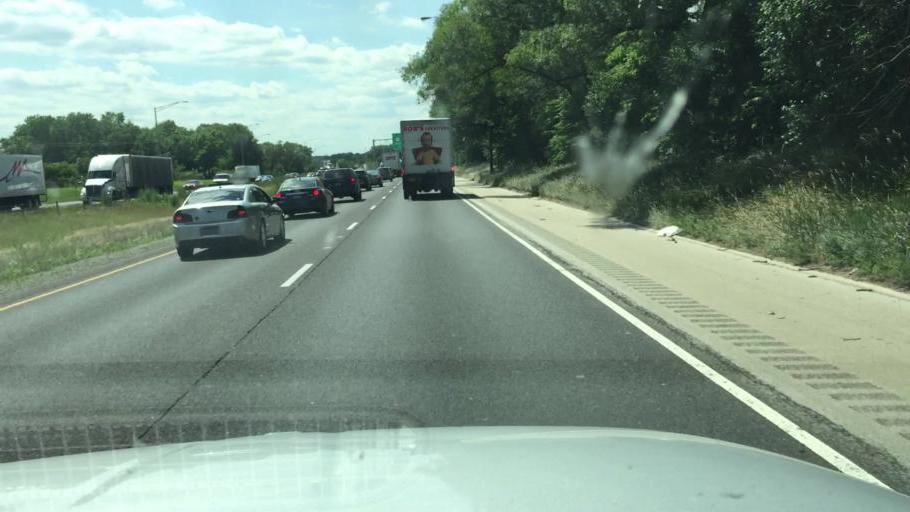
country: US
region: Illinois
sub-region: Will County
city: Joliet
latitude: 41.5134
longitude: -88.0675
